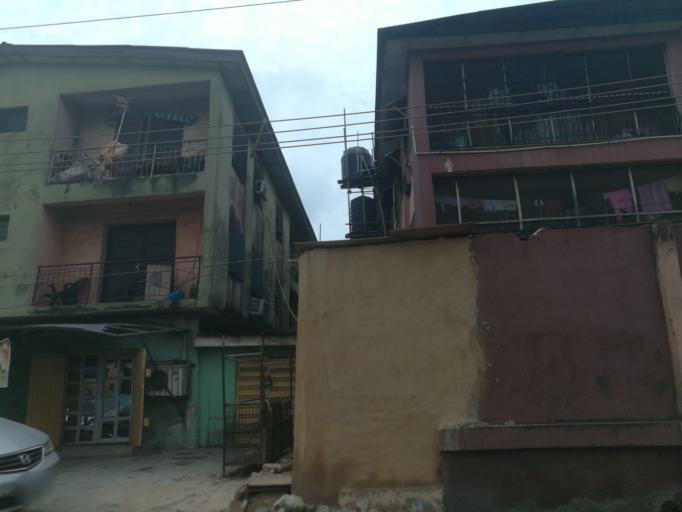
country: NG
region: Lagos
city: Somolu
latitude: 6.5334
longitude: 3.3898
